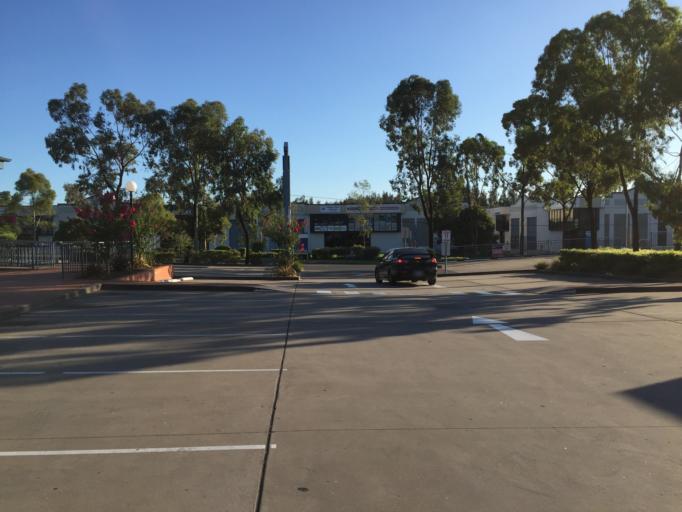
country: AU
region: New South Wales
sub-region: Blacktown
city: Doonside
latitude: -33.7893
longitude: 150.8894
